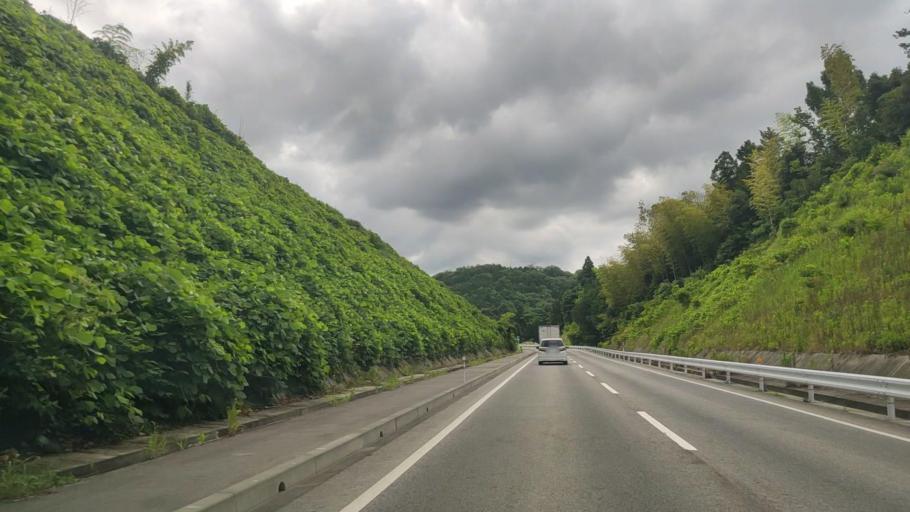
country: JP
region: Tottori
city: Yonago
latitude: 35.3774
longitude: 133.3942
